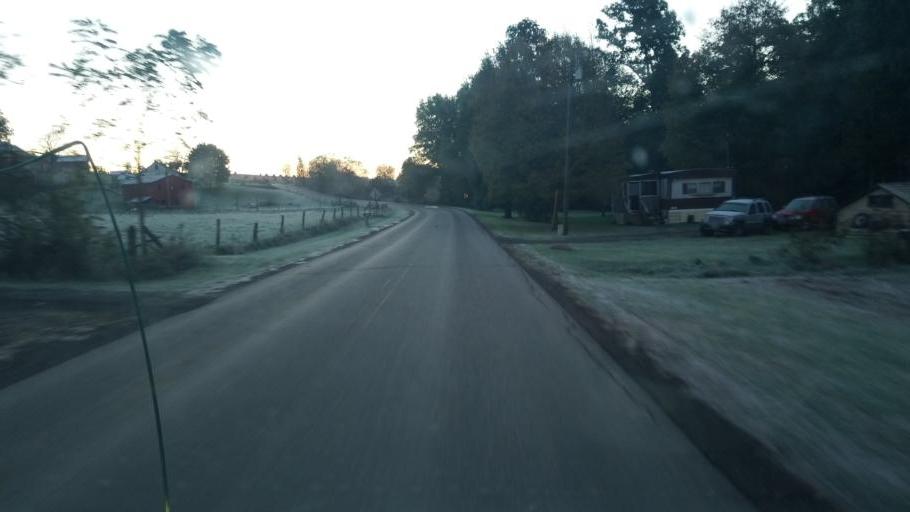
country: US
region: Ohio
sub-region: Wayne County
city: Dalton
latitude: 40.7343
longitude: -81.7245
